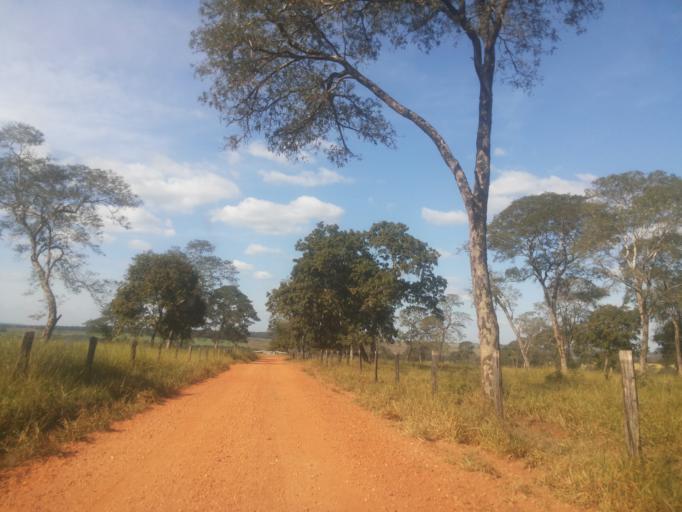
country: BR
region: Minas Gerais
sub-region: Santa Vitoria
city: Santa Vitoria
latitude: -19.0119
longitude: -50.4023
